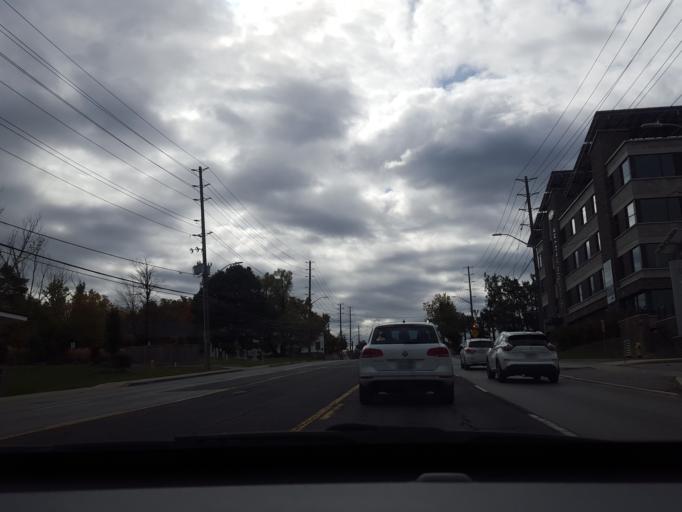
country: CA
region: Ontario
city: Markham
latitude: 43.8456
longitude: -79.3055
